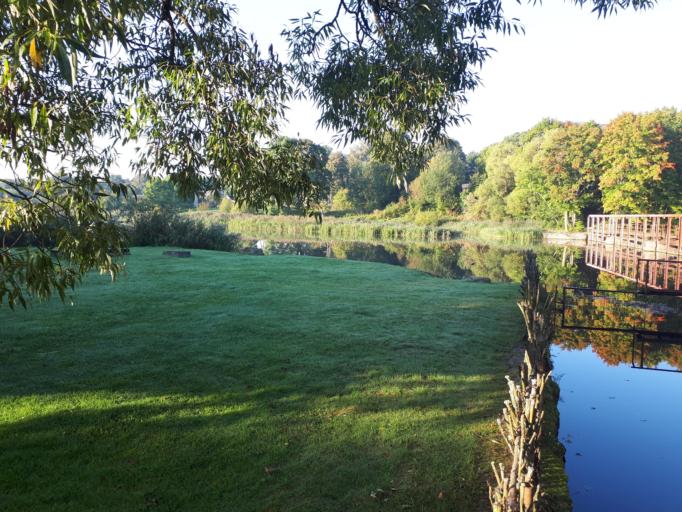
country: LT
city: Vieksniai
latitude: 56.1584
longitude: 22.5325
